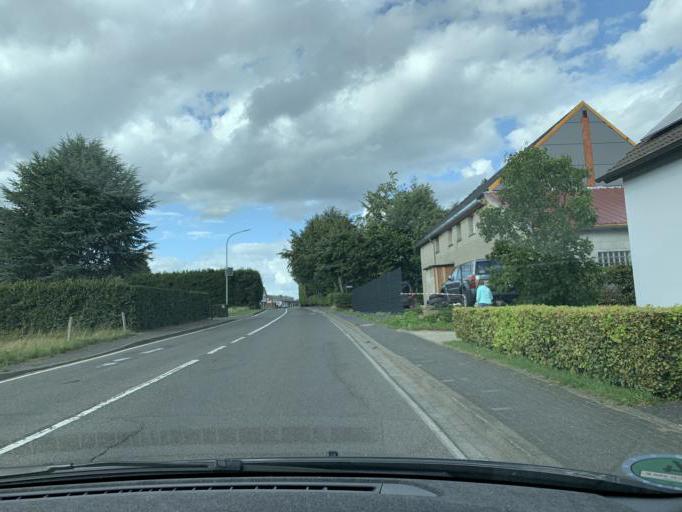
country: DE
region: North Rhine-Westphalia
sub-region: Regierungsbezirk Koln
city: Simmerath
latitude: 50.6134
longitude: 6.3099
